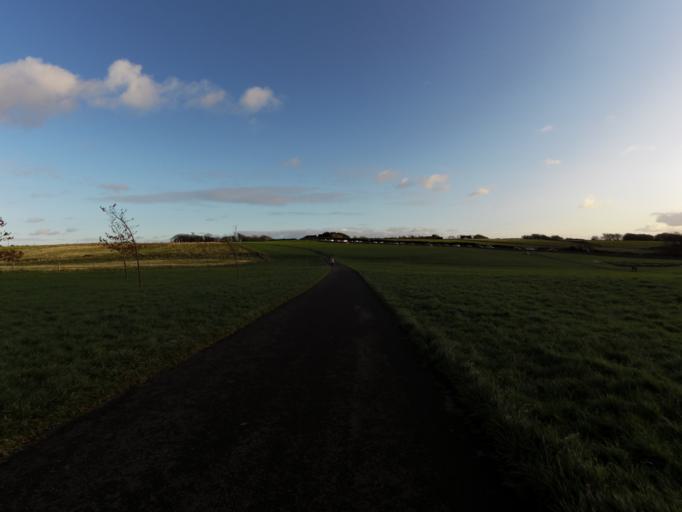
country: IE
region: Connaught
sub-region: County Galway
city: Oranmore
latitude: 53.2470
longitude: -8.9618
